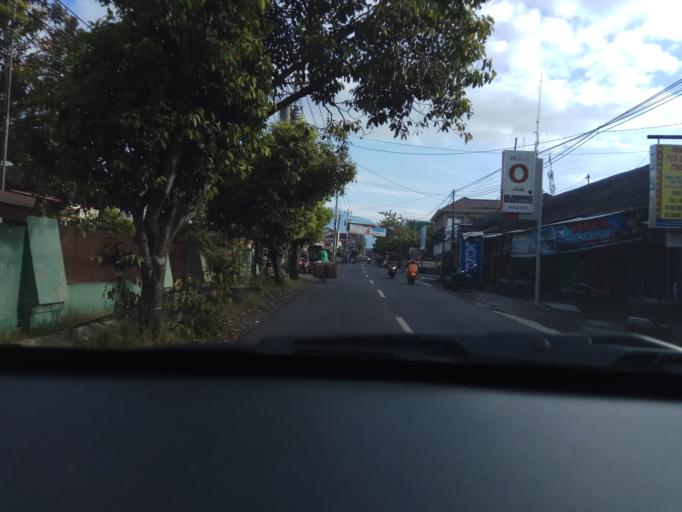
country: ID
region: Daerah Istimewa Yogyakarta
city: Depok
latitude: -7.7627
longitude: 110.4065
